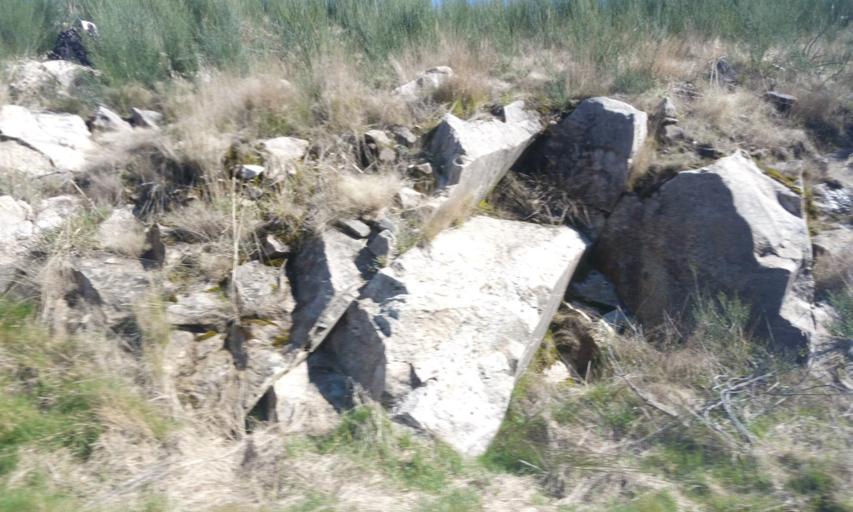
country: PT
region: Guarda
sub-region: Manteigas
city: Manteigas
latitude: 40.4946
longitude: -7.5260
